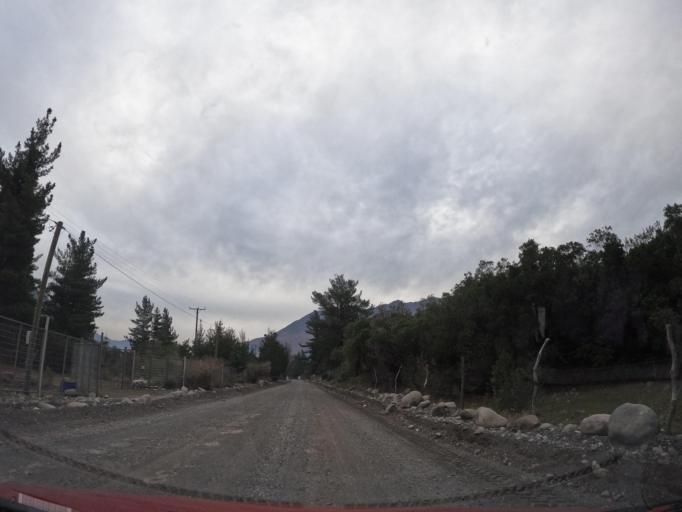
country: CL
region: Maule
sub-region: Provincia de Linares
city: Colbun
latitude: -35.7044
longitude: -71.0845
